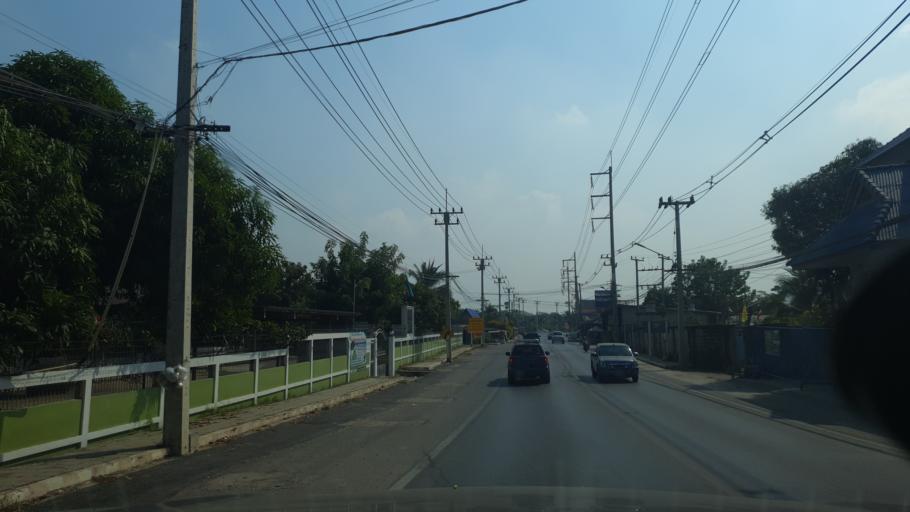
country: TH
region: Nakhon Pathom
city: Salaya
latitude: 13.7738
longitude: 100.2824
